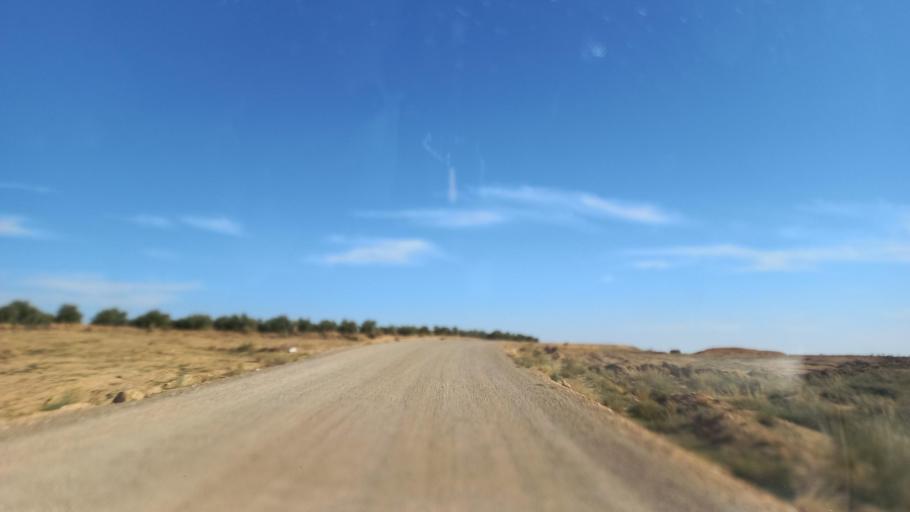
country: TN
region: Al Qasrayn
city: Sbiba
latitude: 35.2999
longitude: 9.0964
